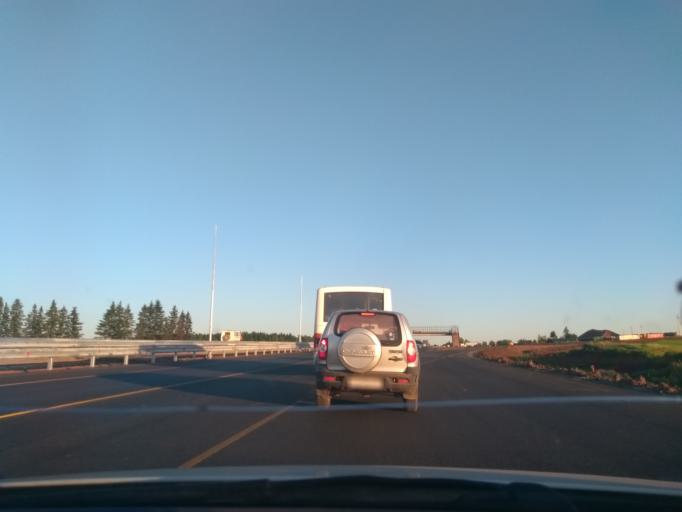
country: RU
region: Perm
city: Lobanovo
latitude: 57.8385
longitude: 56.2976
